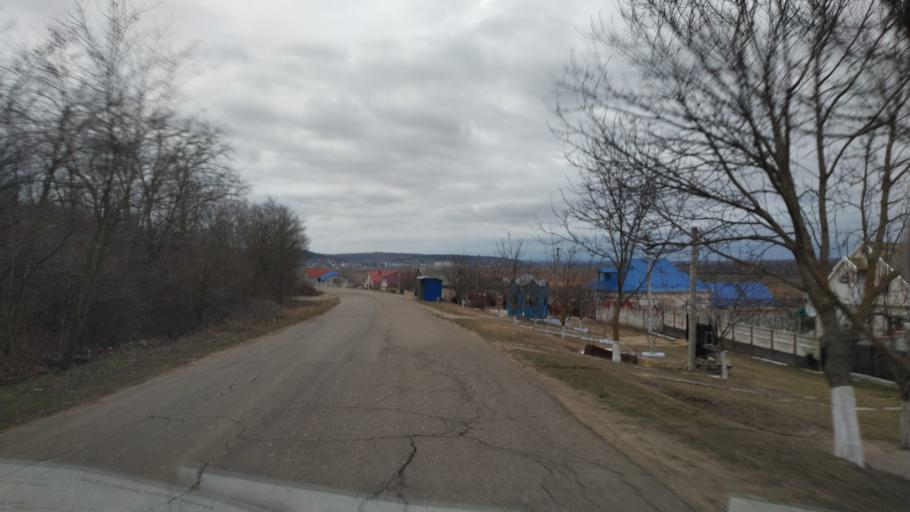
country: MD
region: Causeni
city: Causeni
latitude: 46.6637
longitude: 29.4506
